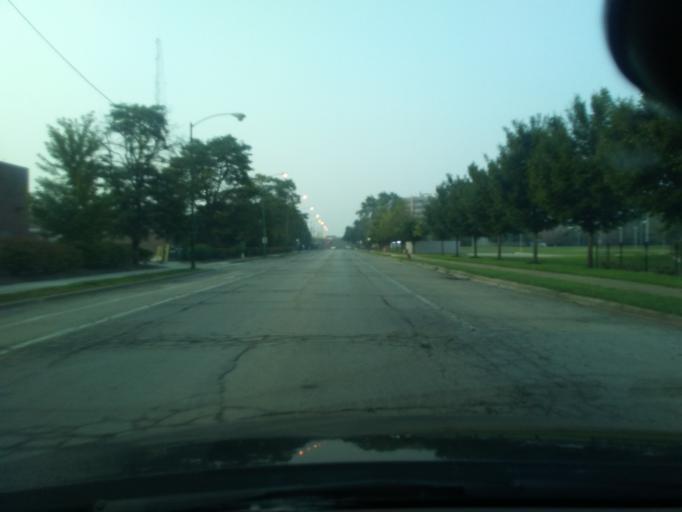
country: US
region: Illinois
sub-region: Cook County
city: Lincolnwood
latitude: 41.9425
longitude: -87.6908
